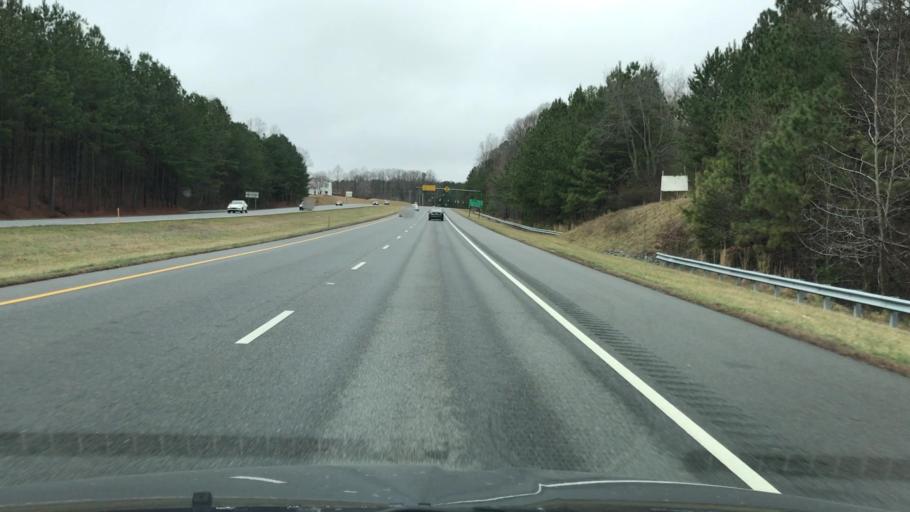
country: US
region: Maryland
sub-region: Calvert County
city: Long Beach
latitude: 38.4661
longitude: -76.5080
